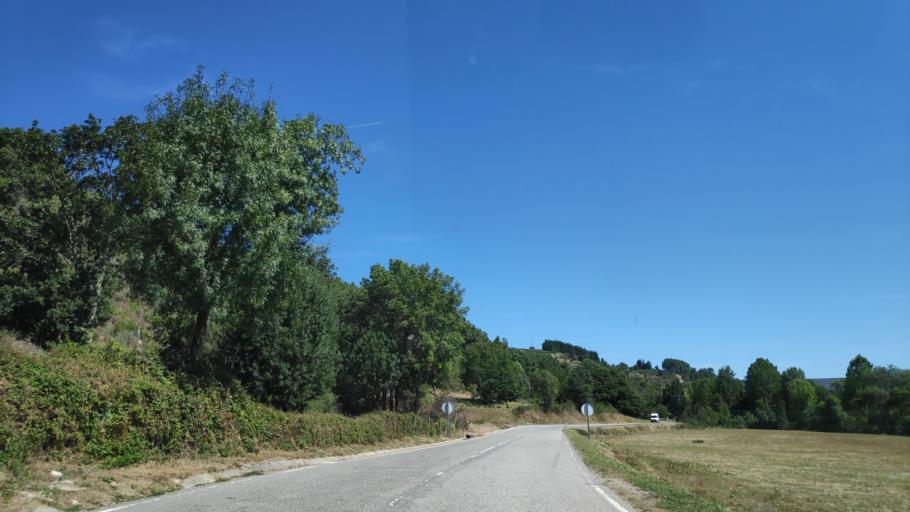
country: PT
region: Braganca
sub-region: Braganca Municipality
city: Braganca
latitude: 41.8772
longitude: -6.7444
